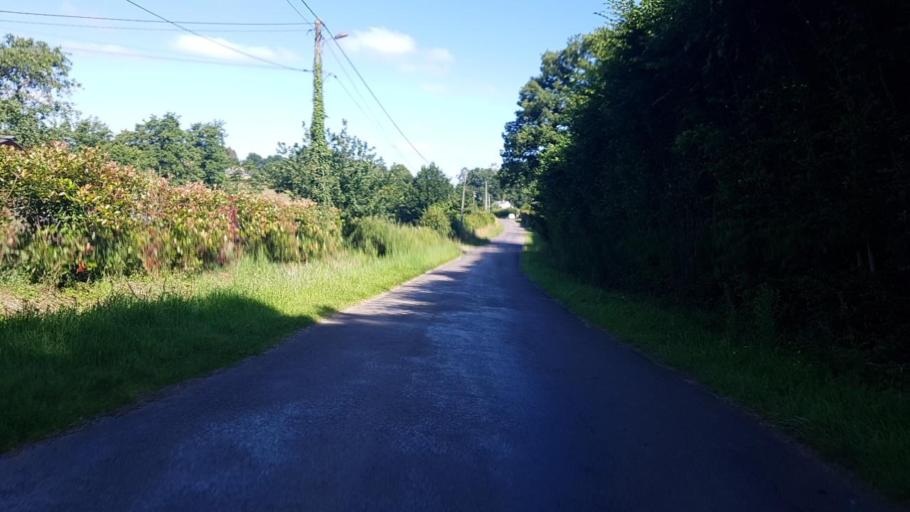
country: FR
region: Nord-Pas-de-Calais
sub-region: Departement du Nord
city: Anor
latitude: 49.9825
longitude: 4.1281
